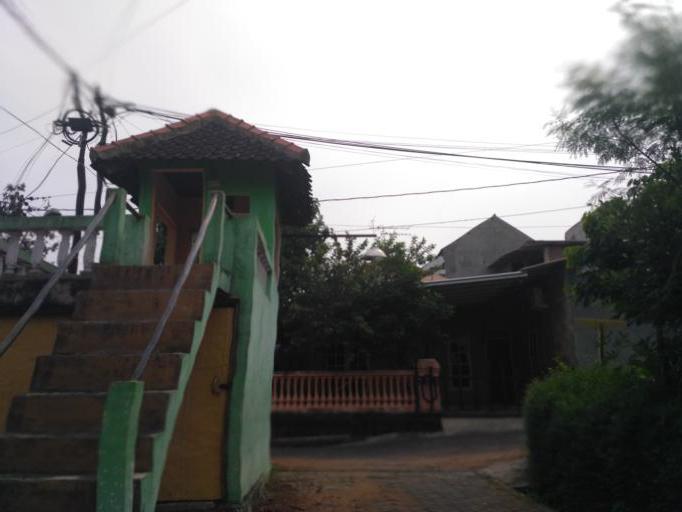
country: ID
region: Central Java
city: Ungaran
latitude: -7.0752
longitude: 110.4321
